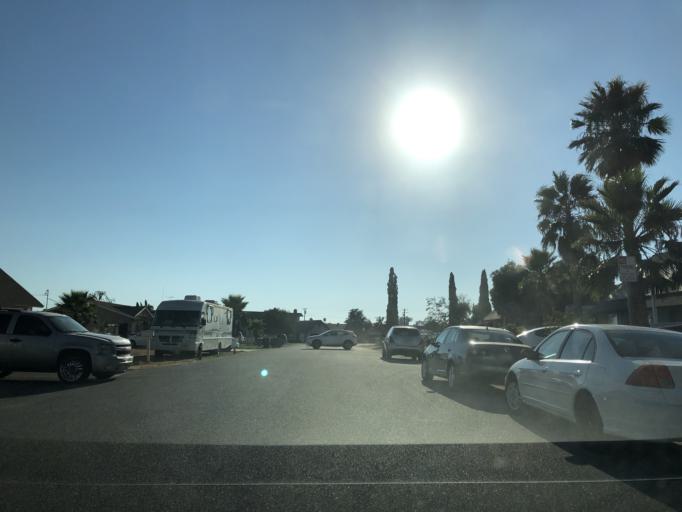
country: US
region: California
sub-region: Riverside County
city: Norco
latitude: 33.9107
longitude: -117.5763
